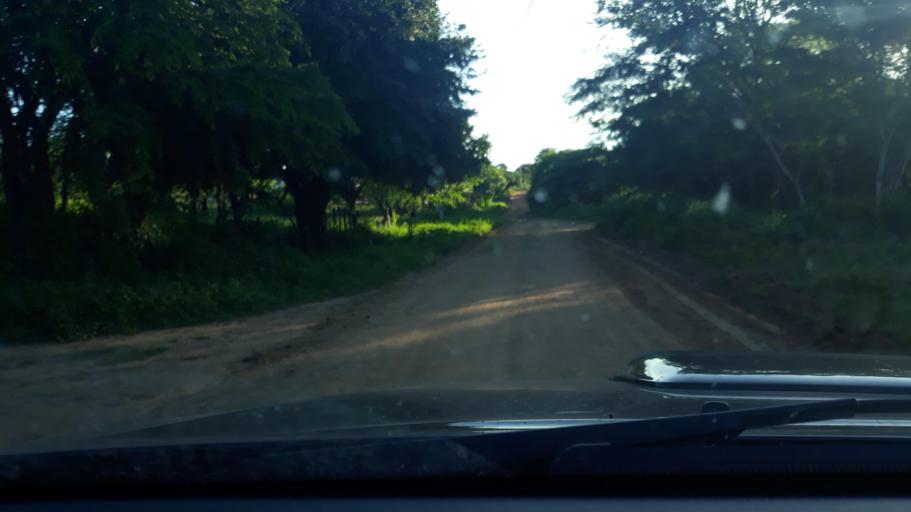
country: BR
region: Bahia
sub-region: Riacho De Santana
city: Riacho de Santana
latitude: -13.8386
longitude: -42.7336
